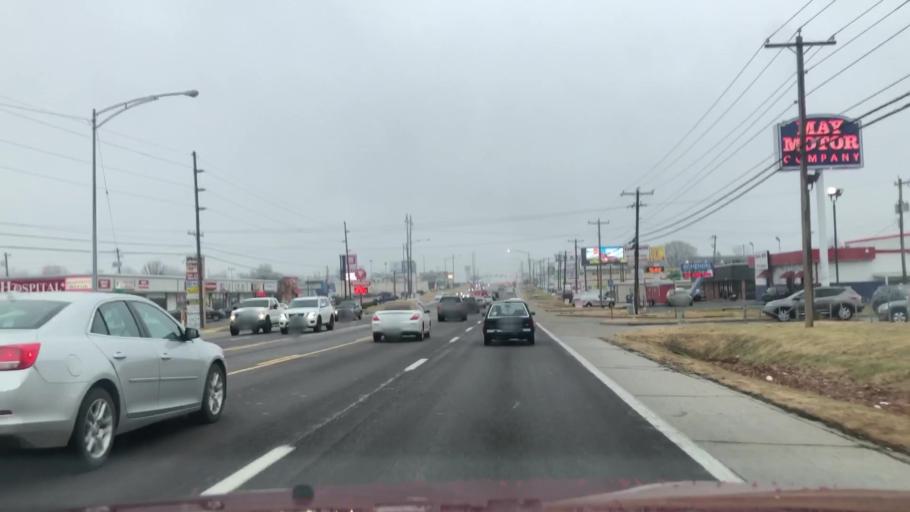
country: US
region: Missouri
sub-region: Greene County
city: Springfield
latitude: 37.1552
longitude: -93.2956
